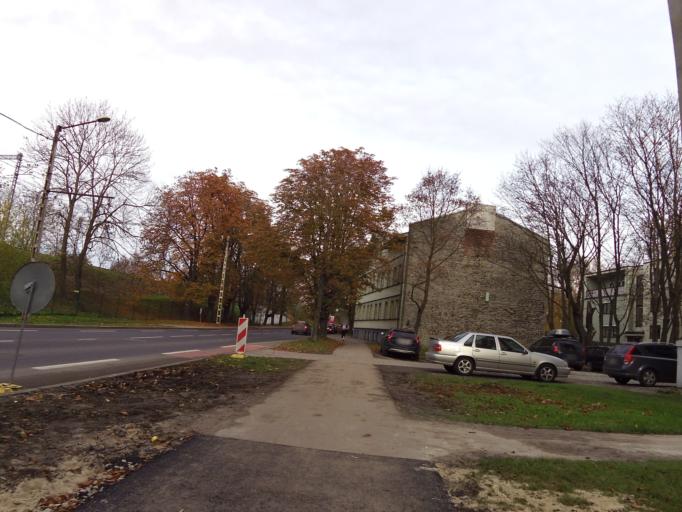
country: EE
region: Harju
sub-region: Tallinna linn
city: Tallinn
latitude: 59.4330
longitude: 24.7237
